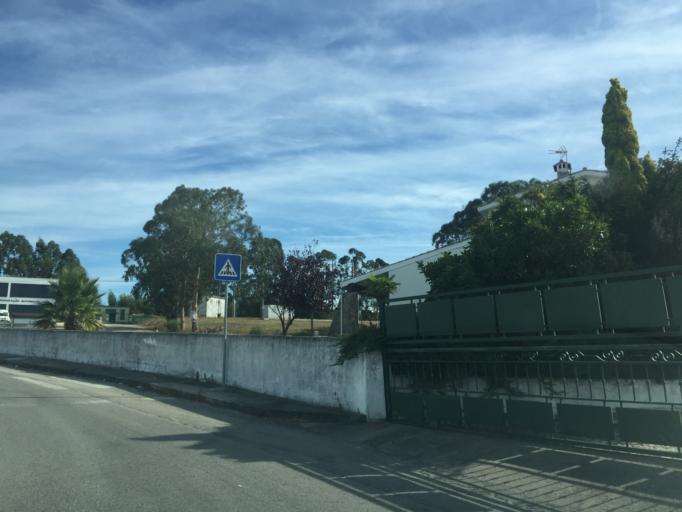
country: PT
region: Coimbra
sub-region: Figueira da Foz
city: Lavos
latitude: 40.0844
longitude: -8.8249
